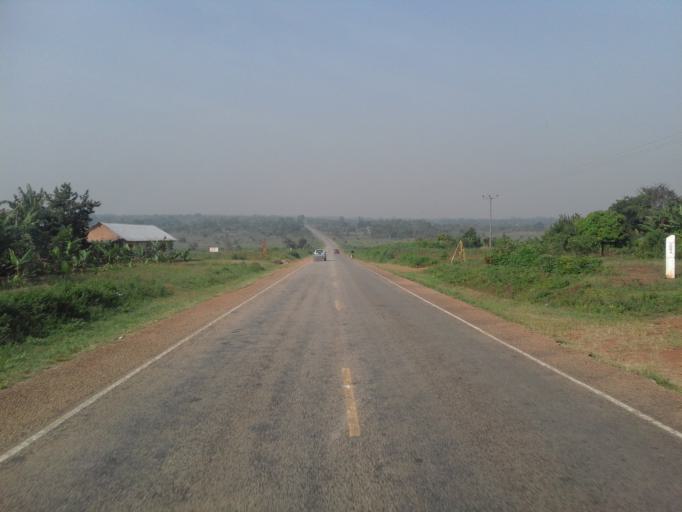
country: UG
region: Eastern Region
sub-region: Budaka District
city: Budaka
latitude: 1.0349
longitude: 33.9966
